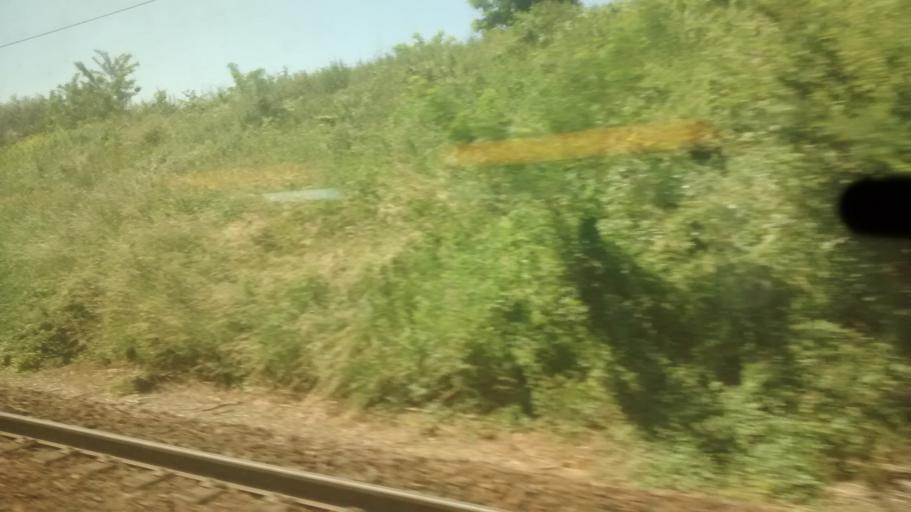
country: FR
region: Rhone-Alpes
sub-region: Departement du Rhone
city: Sathonay-Village
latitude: 45.8371
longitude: 4.8913
